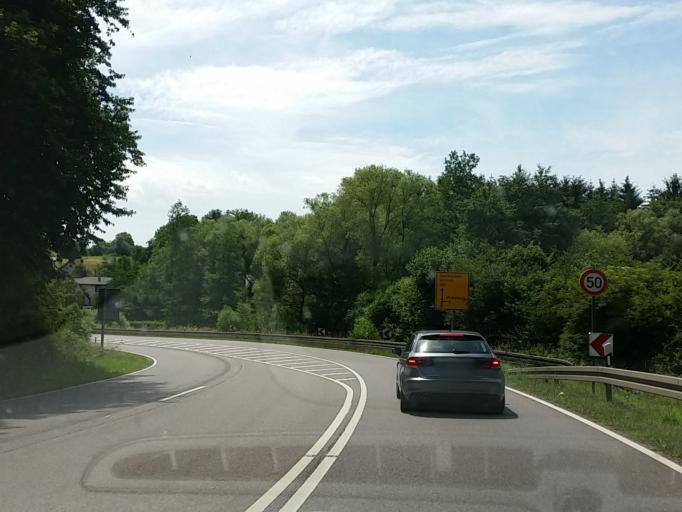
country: DE
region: Saarland
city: Schmelz
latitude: 49.4635
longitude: 6.8427
